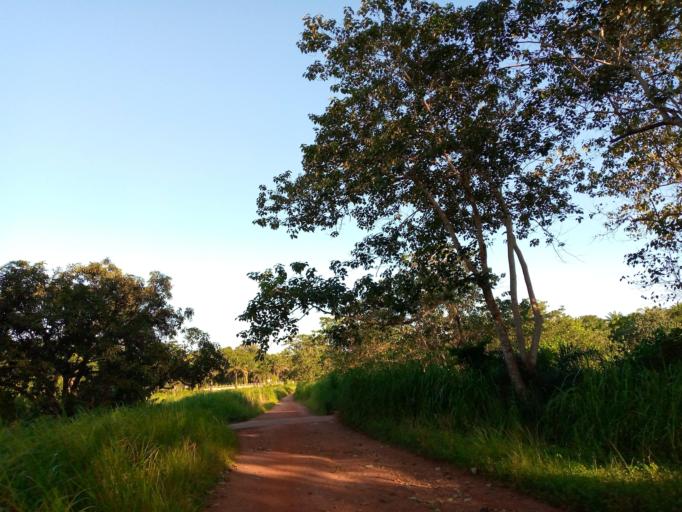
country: SL
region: Northern Province
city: Yonibana
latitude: 8.4494
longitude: -12.2431
